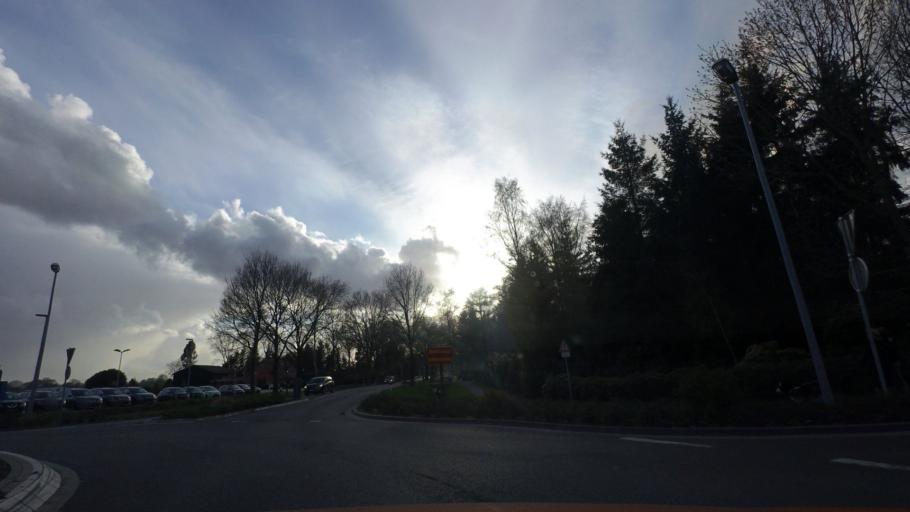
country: DE
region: Lower Saxony
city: Edewecht
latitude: 53.1244
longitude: 8.0832
